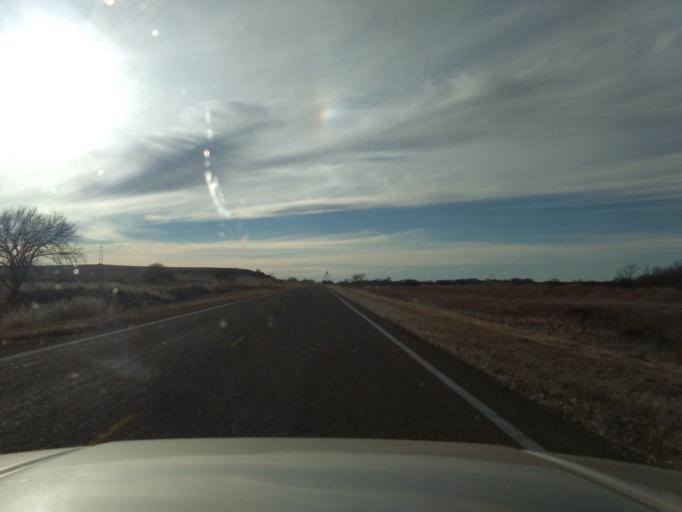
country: US
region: Kansas
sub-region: Norton County
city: Norton
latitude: 39.7440
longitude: -100.1620
